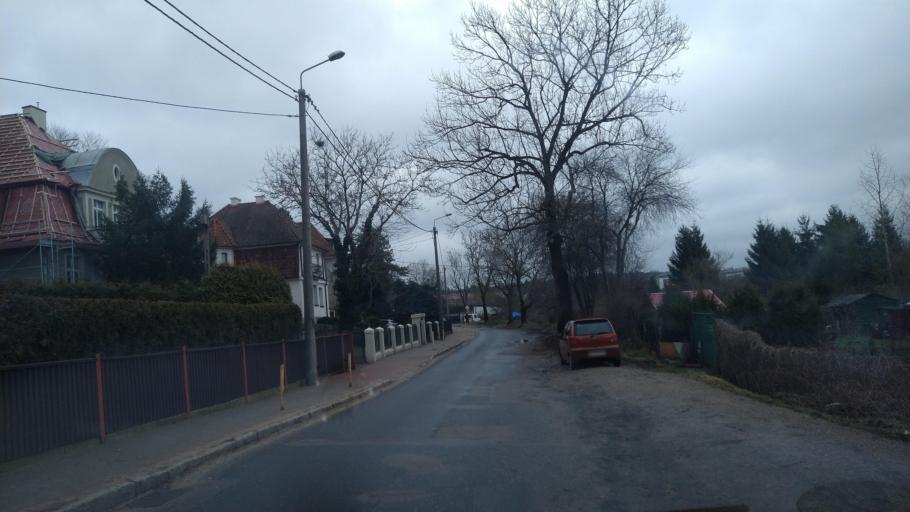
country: PL
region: Warmian-Masurian Voivodeship
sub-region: Powiat olsztynski
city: Olsztyn
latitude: 53.7976
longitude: 20.4835
